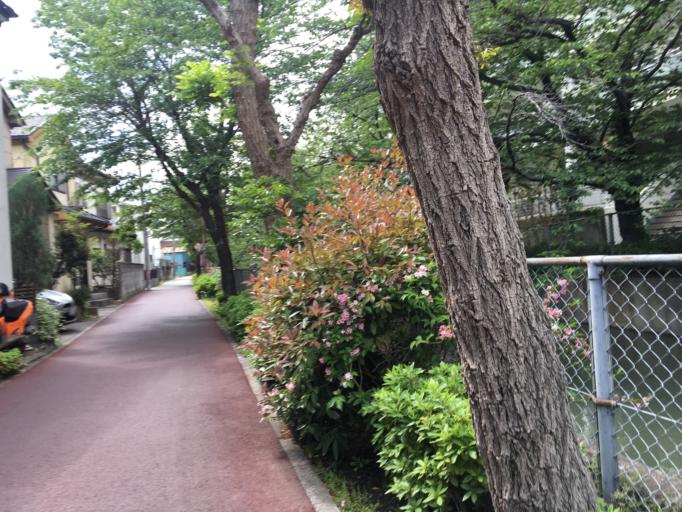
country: JP
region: Saitama
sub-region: Kawaguchi-shi
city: Hatogaya-honcho
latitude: 35.8303
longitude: 139.7429
